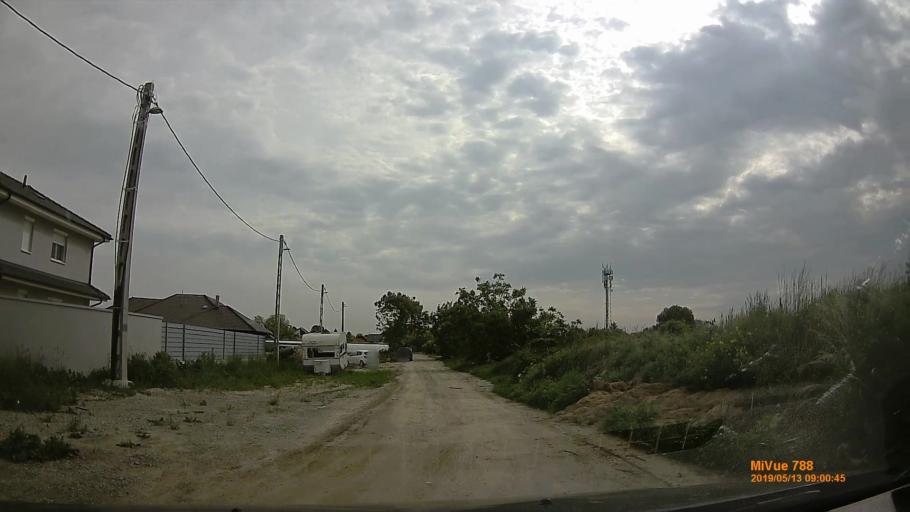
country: HU
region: Budapest
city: Budapest XXI. keruelet
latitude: 47.4013
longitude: 19.0817
